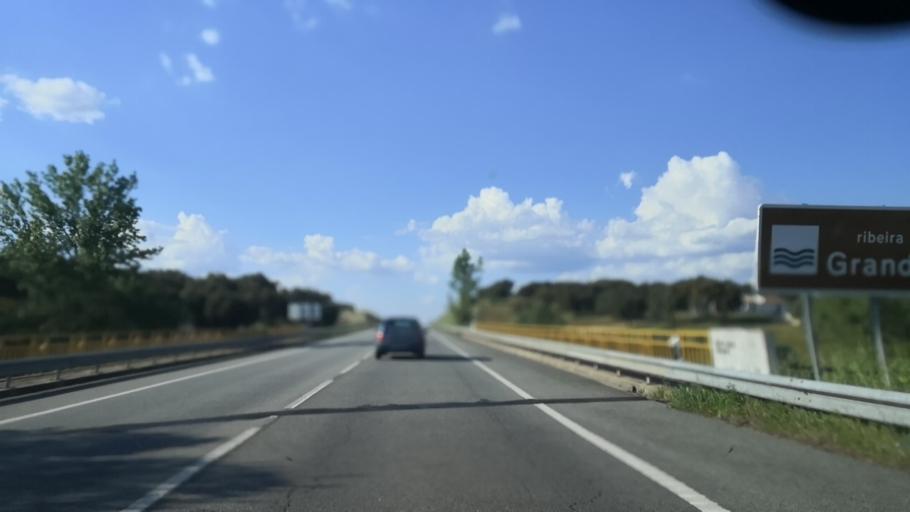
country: PT
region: Portalegre
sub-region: Arronches
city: Arronches
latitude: 39.0680
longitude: -7.4356
